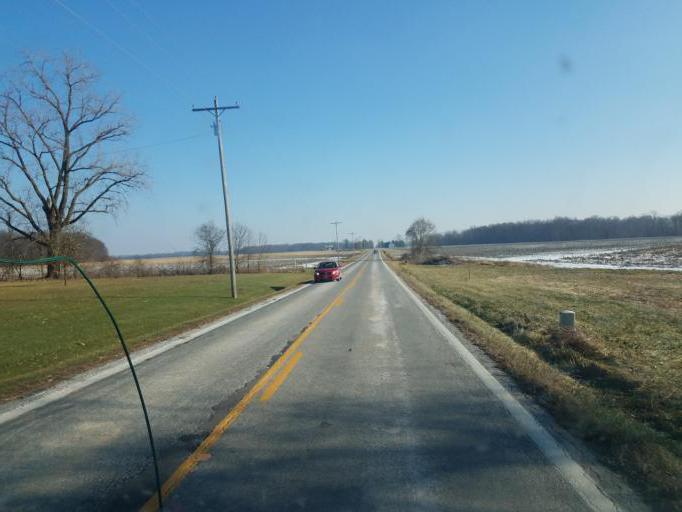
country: US
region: Ohio
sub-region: Morrow County
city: Cardington
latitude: 40.5398
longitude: -83.0059
